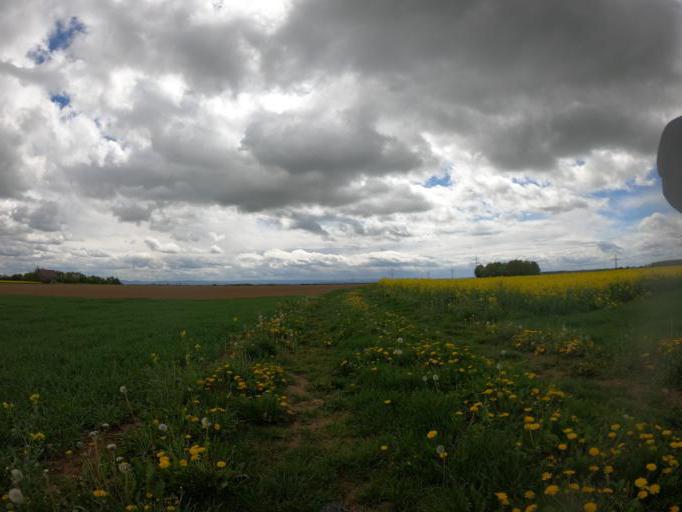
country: DE
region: Baden-Wuerttemberg
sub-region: Regierungsbezirk Stuttgart
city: Oberjettingen
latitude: 48.5805
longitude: 8.7946
